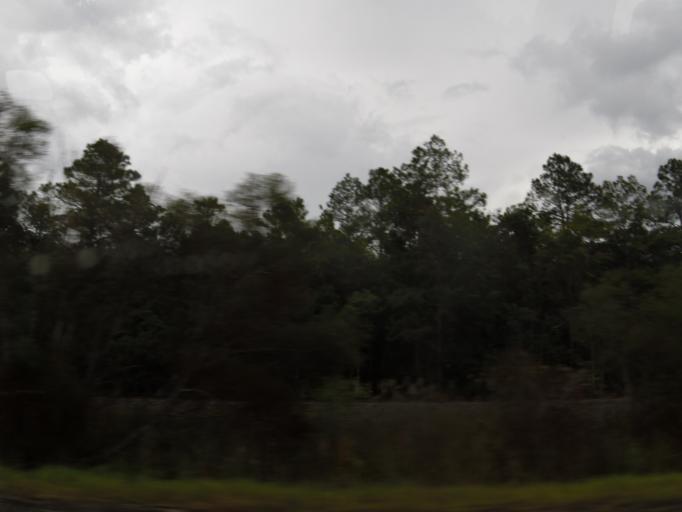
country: US
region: Georgia
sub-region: Wayne County
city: Jesup
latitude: 31.4486
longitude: -81.6955
